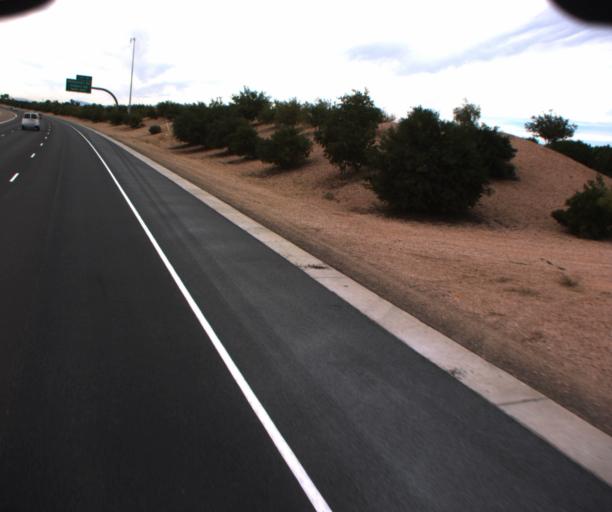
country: US
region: Arizona
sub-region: Maricopa County
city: Mesa
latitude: 33.4783
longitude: -111.7745
